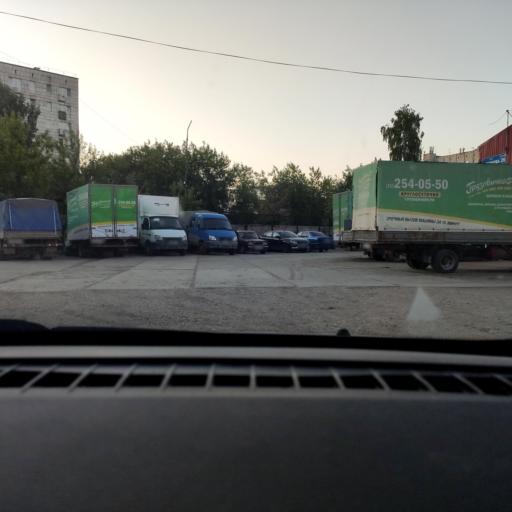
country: RU
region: Perm
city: Perm
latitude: 57.9710
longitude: 56.2350
